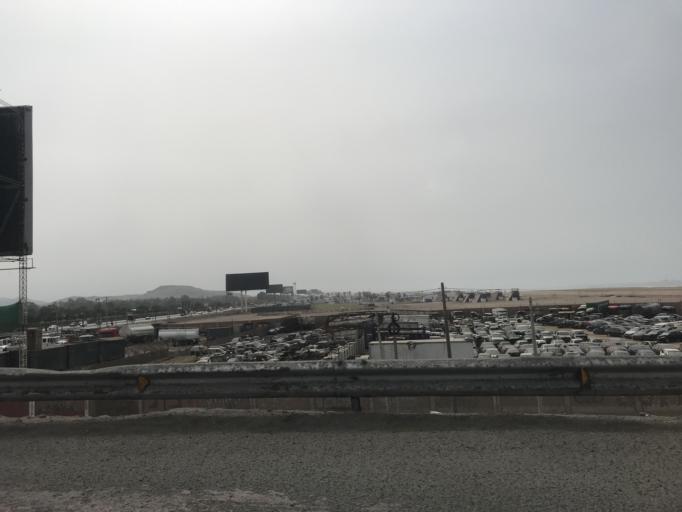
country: PE
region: Lima
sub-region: Lima
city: Punta Hermosa
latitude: -12.2571
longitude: -76.9220
